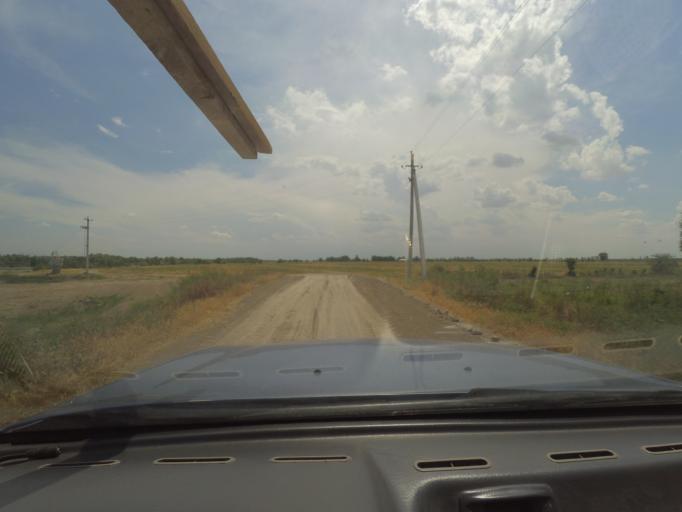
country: TJ
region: Viloyati Sughd
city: Buston
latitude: 40.5456
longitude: 69.0785
